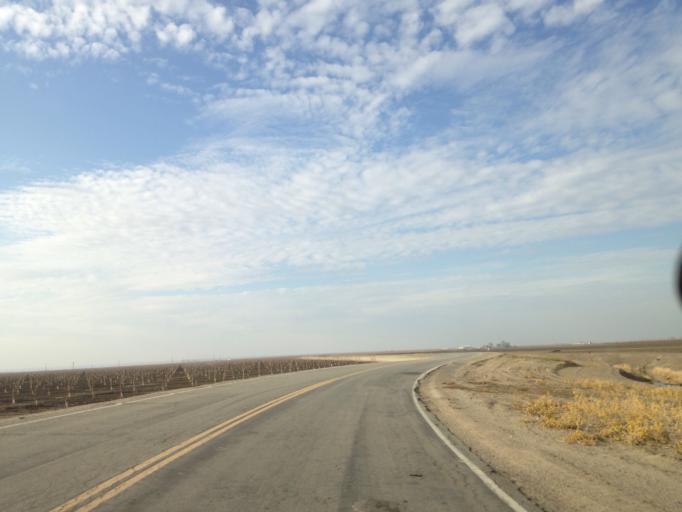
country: US
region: California
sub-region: Kern County
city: Buttonwillow
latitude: 35.4438
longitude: -119.5522
